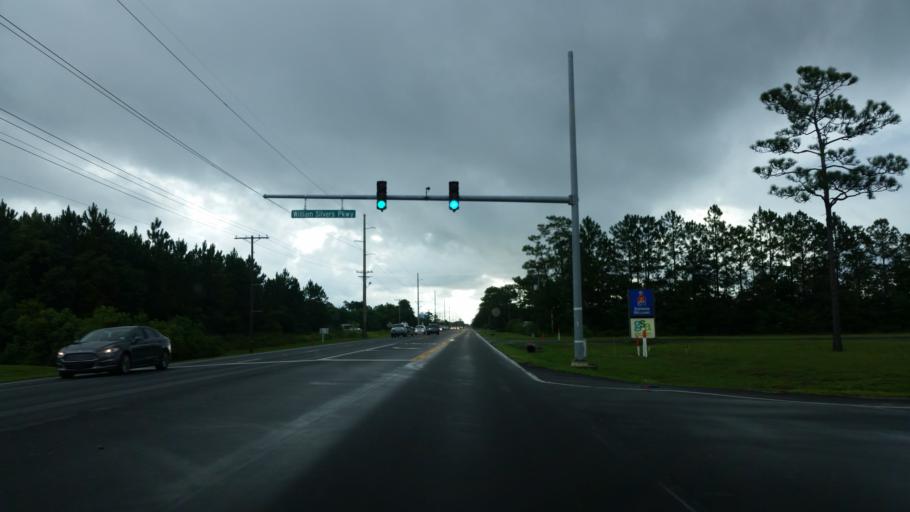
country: US
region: Alabama
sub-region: Baldwin County
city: Orange Beach
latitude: 30.2902
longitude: -87.6152
